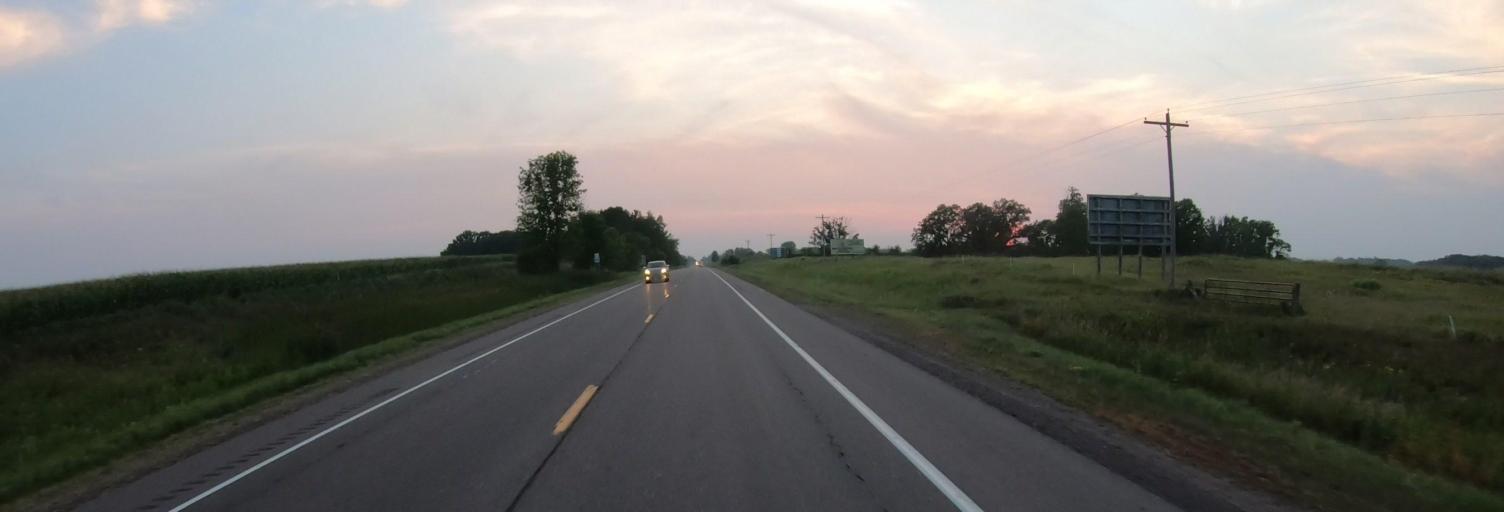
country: US
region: Minnesota
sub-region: Pine County
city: Rock Creek
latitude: 45.7666
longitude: -92.9730
